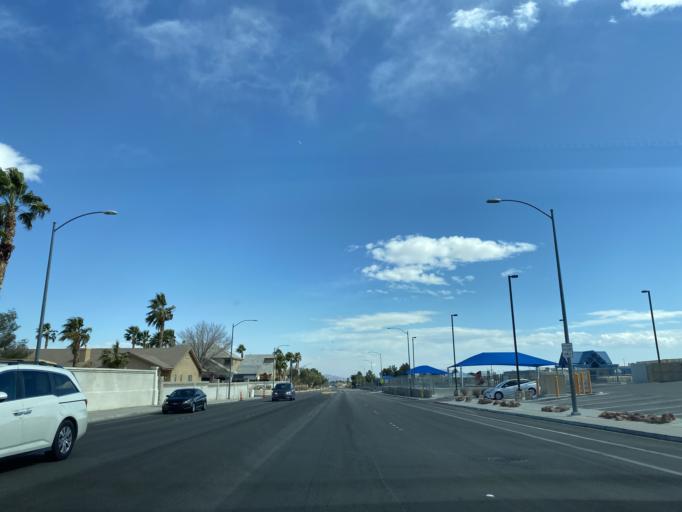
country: US
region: Nevada
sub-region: Clark County
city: Spring Valley
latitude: 36.2259
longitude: -115.2669
